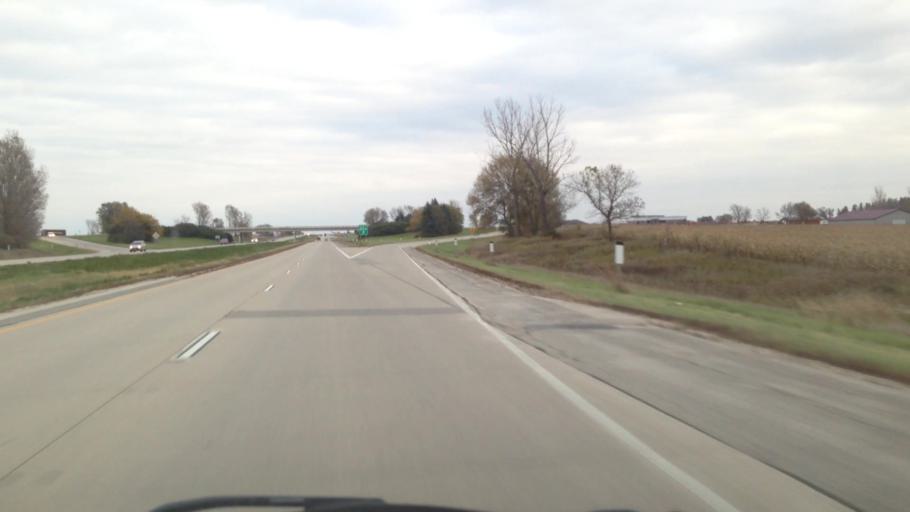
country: US
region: Minnesota
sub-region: Olmsted County
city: Eyota
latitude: 43.9549
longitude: -92.2448
